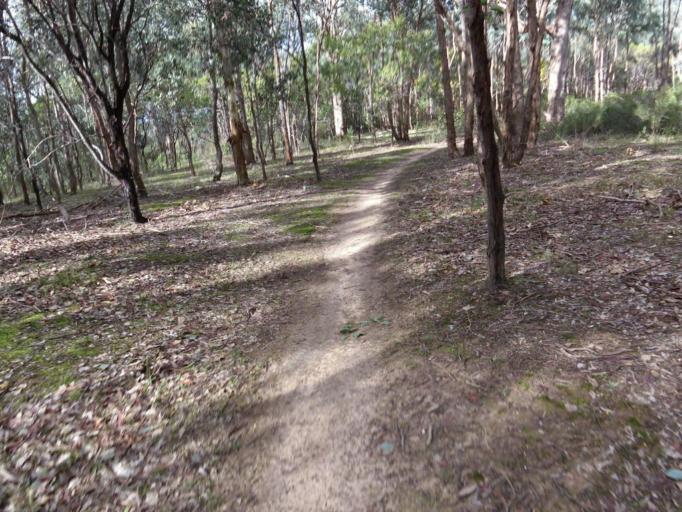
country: AU
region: Victoria
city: Plenty
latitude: -37.6688
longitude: 145.1069
